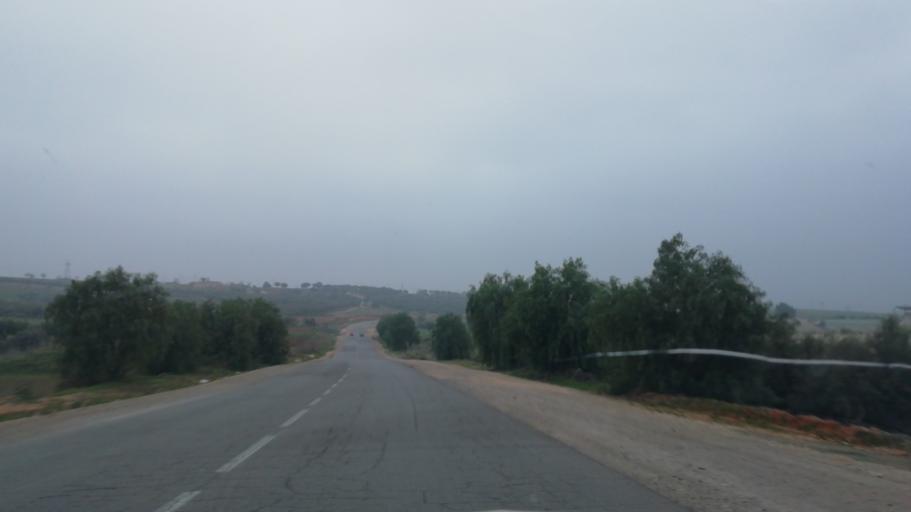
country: DZ
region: Mascara
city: Mascara
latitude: 35.3906
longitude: 0.1608
